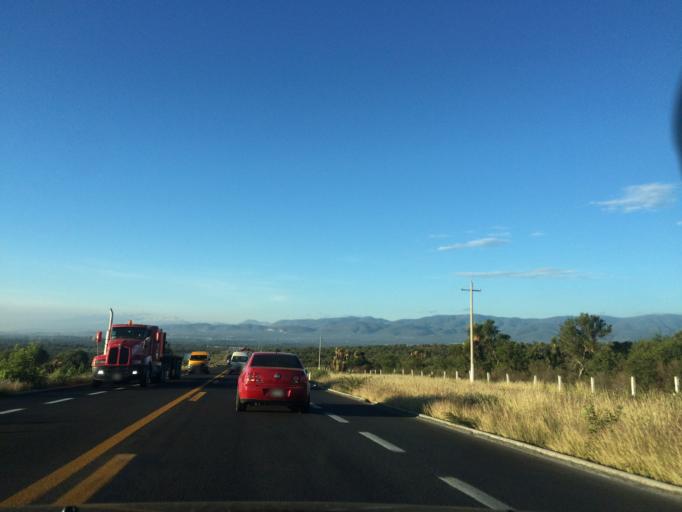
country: MX
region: Puebla
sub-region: Tehuacan
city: Magdalena Cuayucatepec
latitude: 18.5694
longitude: -97.4640
